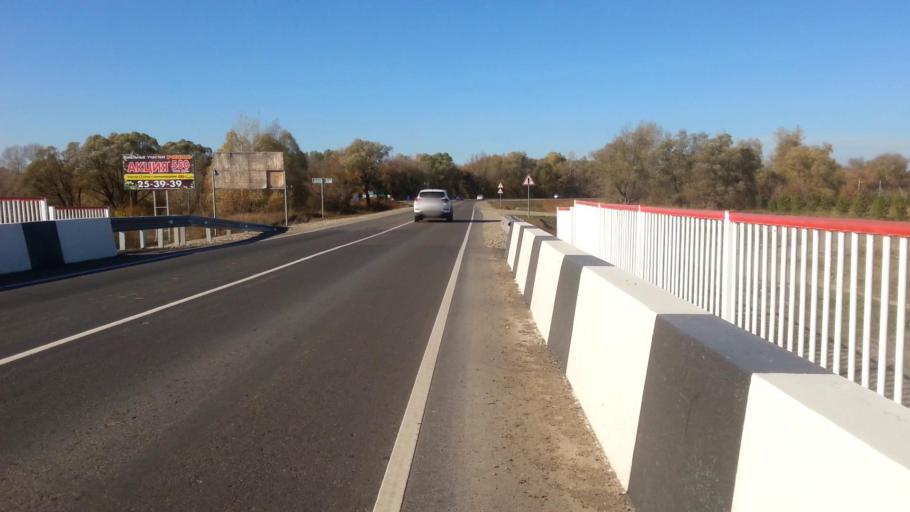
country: RU
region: Altai Krai
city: Sannikovo
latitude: 53.3202
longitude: 83.9439
